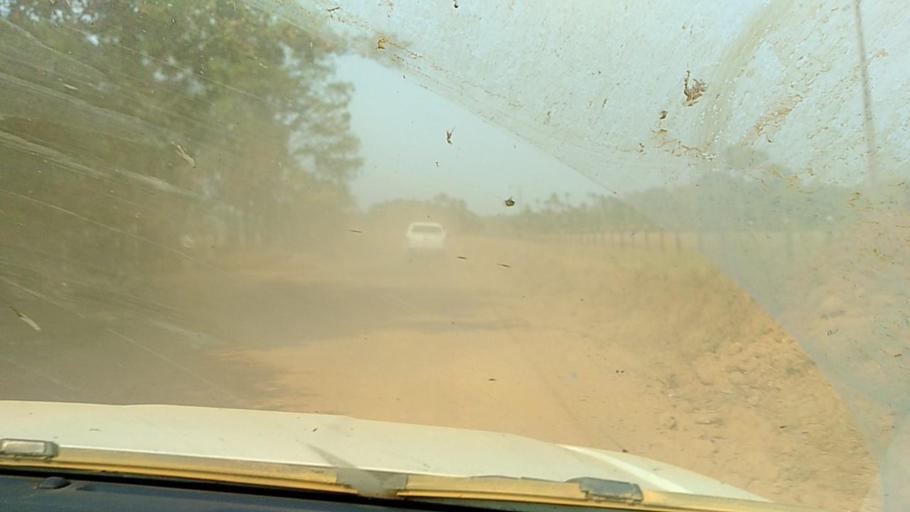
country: BR
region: Rondonia
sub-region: Porto Velho
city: Porto Velho
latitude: -8.7851
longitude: -64.0907
